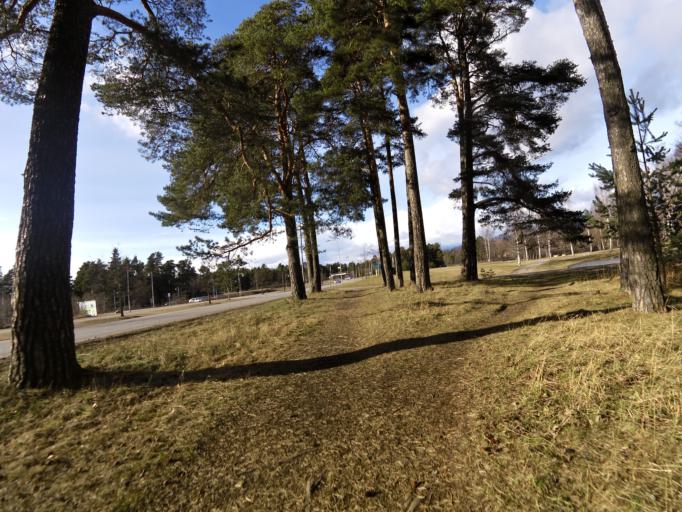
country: SE
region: Gaevleborg
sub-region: Gavle Kommun
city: Gavle
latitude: 60.6719
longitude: 17.1089
